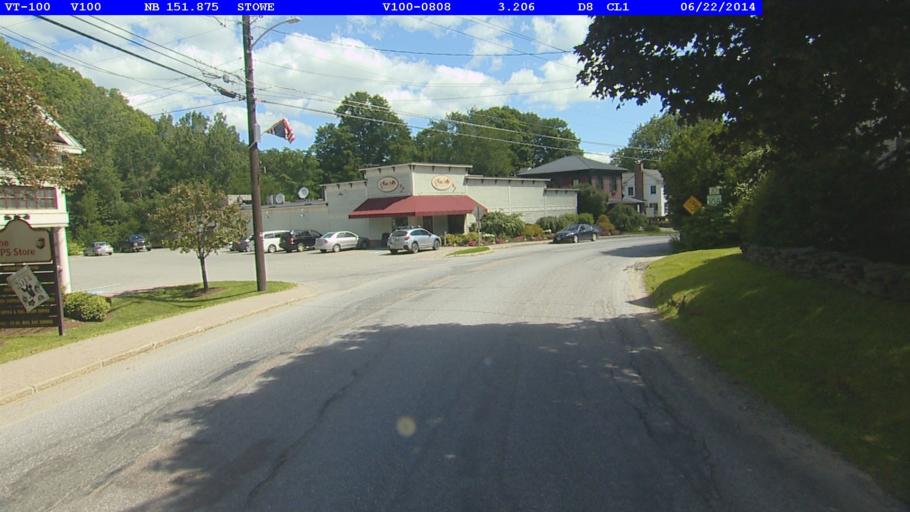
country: US
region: Vermont
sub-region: Lamoille County
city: Morristown
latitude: 44.4648
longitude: -72.6895
